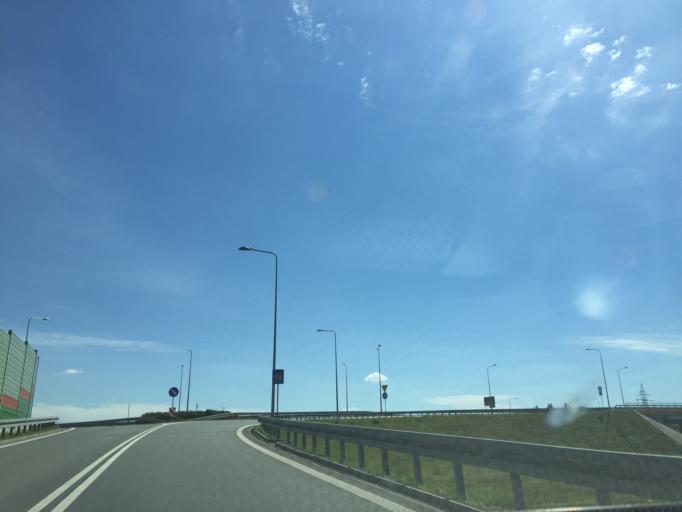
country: PL
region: Lodz Voivodeship
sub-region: Piotrkow Trybunalski
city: Piotrkow Trybunalski
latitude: 51.4446
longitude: 19.7222
